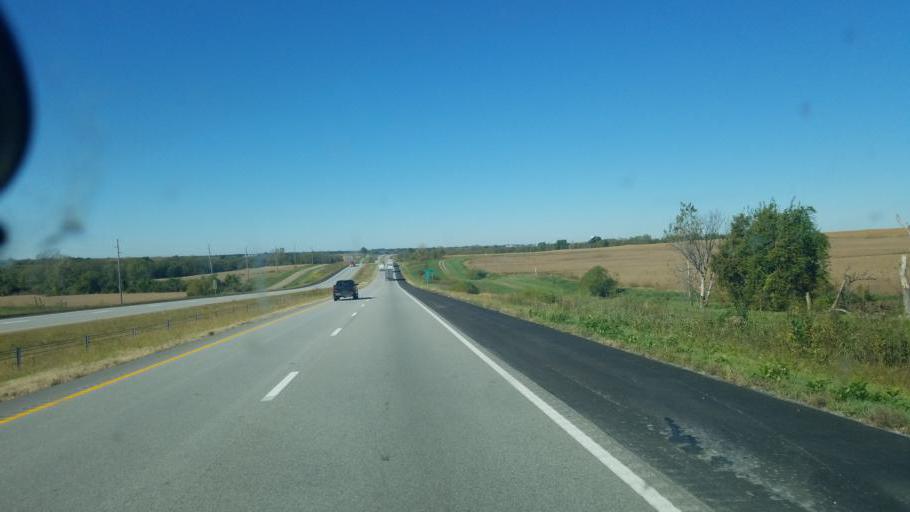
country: US
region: Missouri
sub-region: Lafayette County
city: Higginsville
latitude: 38.9927
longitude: -93.6882
